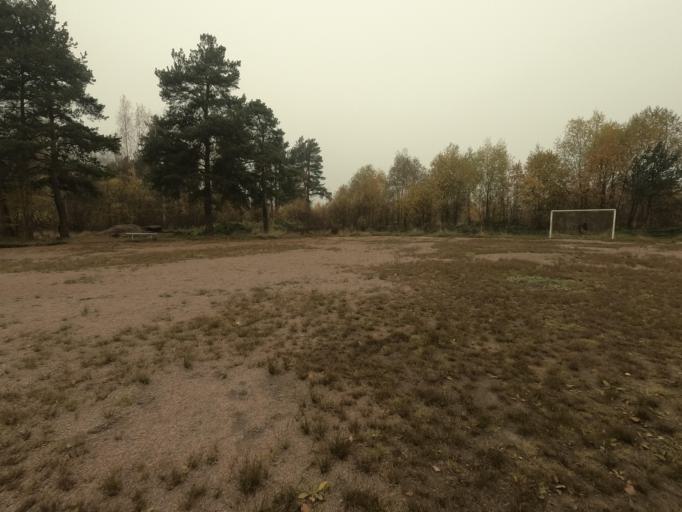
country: RU
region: Leningrad
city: Pavlovo
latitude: 59.7652
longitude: 30.9608
